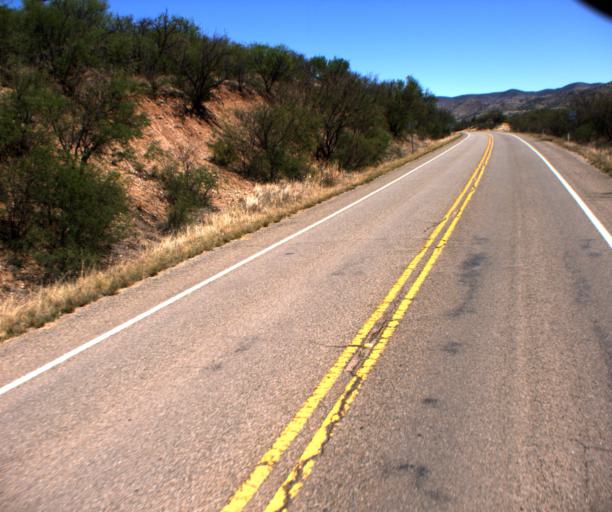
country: US
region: Arizona
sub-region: Santa Cruz County
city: Rio Rico
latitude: 31.5470
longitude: -110.7426
